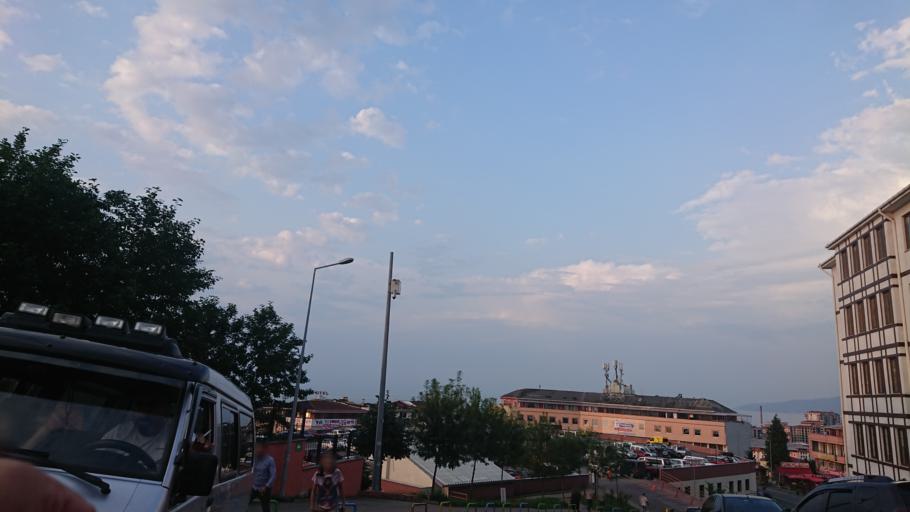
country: TR
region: Rize
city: Gundogdu
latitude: 41.0382
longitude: 40.5718
